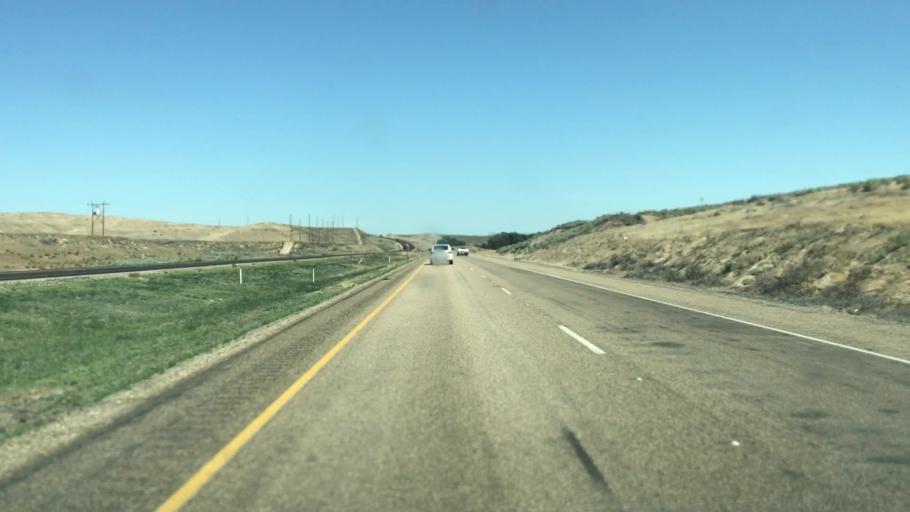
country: US
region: Idaho
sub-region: Payette County
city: New Plymouth
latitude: 43.8914
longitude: -116.8046
